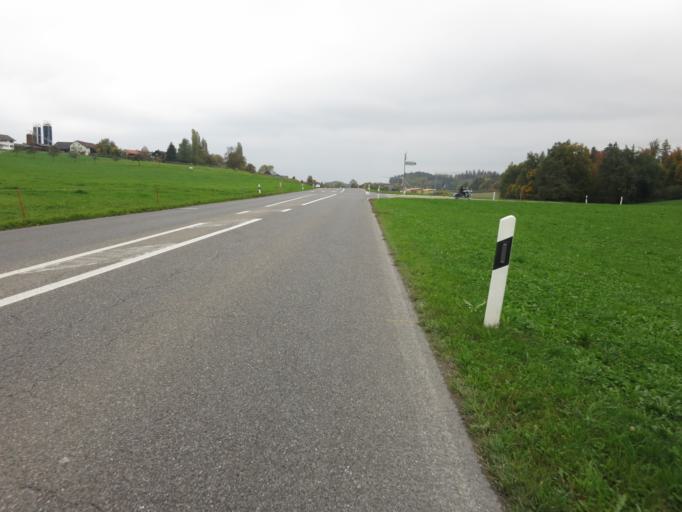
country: CH
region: Zurich
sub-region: Bezirk Hinwil
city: Bubikon
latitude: 47.2818
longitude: 8.8085
